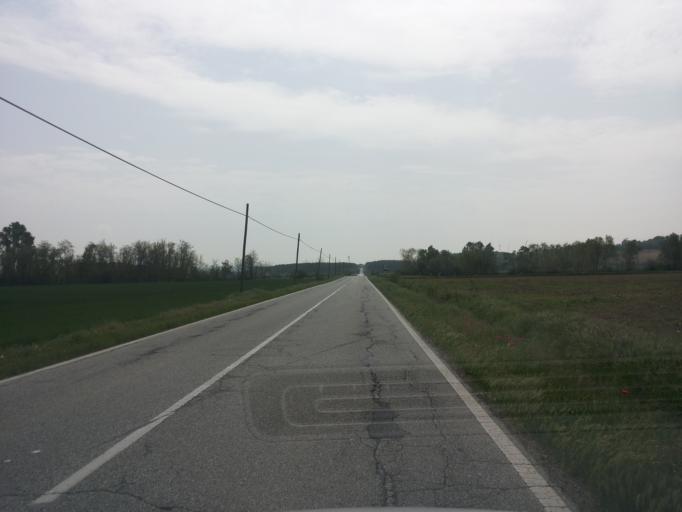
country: IT
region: Piedmont
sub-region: Provincia di Alessandria
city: Occimiano
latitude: 45.0520
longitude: 8.5152
